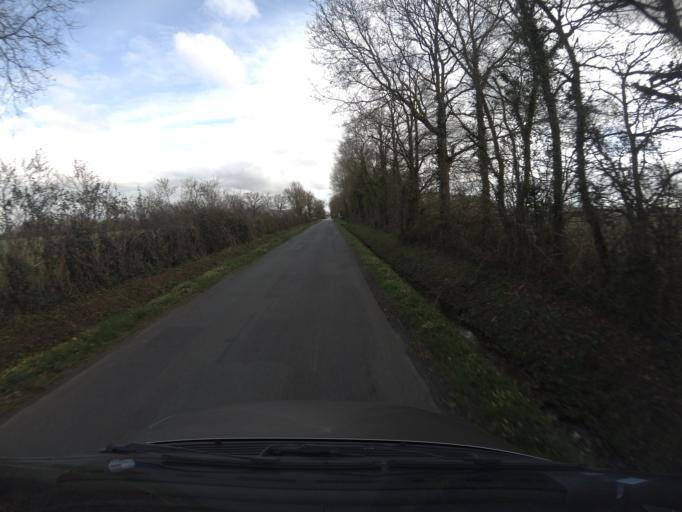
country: FR
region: Pays de la Loire
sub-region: Departement de la Vendee
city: Bouffere
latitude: 46.9683
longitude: -1.3400
